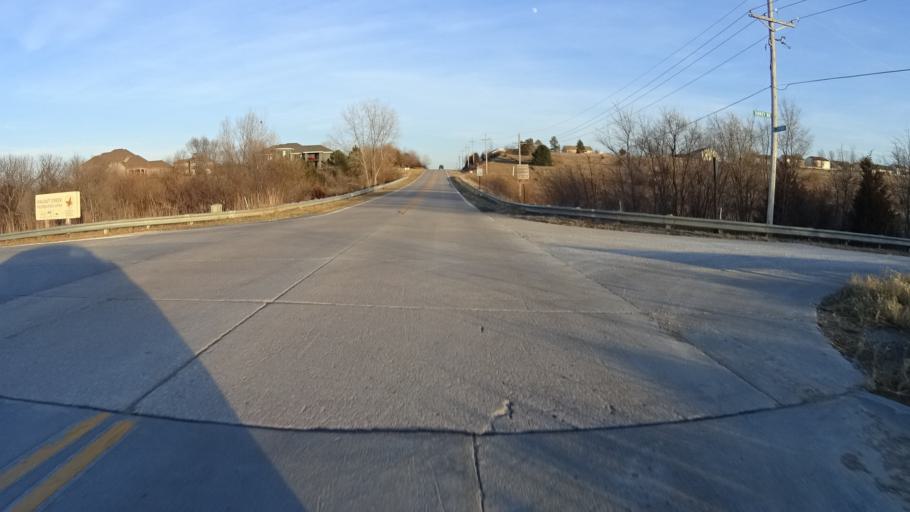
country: US
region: Nebraska
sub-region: Sarpy County
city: Papillion
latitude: 41.1326
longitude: -96.0753
